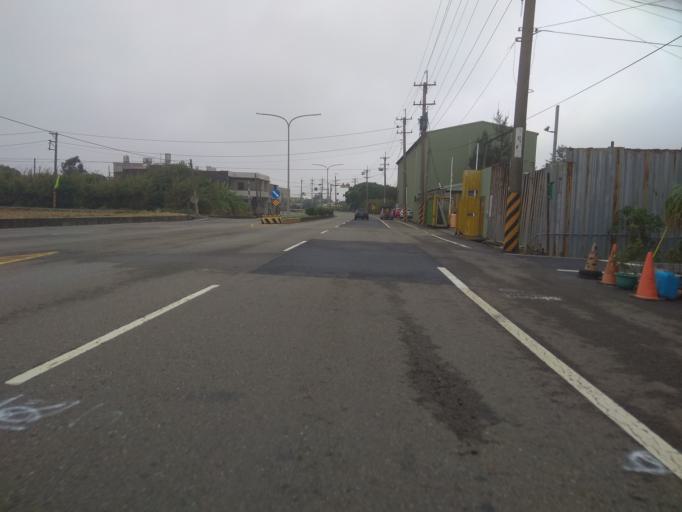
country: TW
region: Taiwan
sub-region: Hsinchu
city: Zhubei
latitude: 24.9993
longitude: 121.0359
